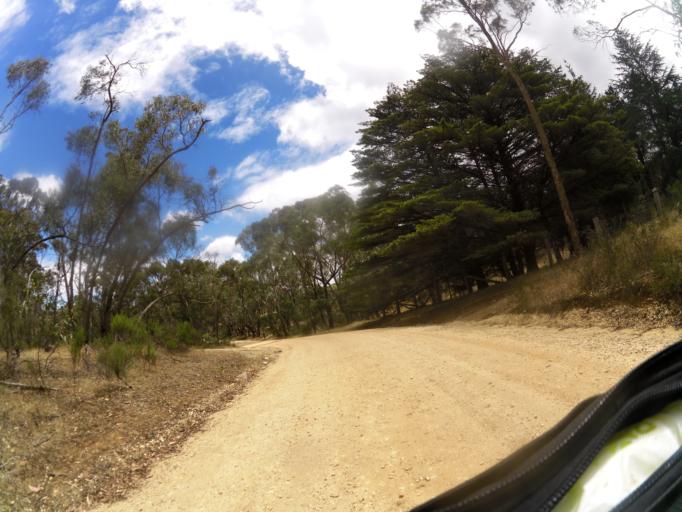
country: AU
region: Victoria
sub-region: Mount Alexander
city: Castlemaine
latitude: -37.0316
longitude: 144.2616
